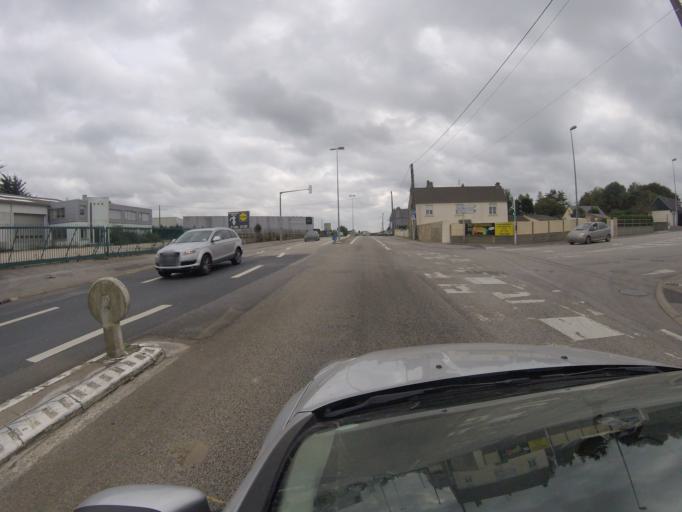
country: FR
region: Lower Normandy
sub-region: Departement de la Manche
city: La Glacerie
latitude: 49.6089
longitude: -1.6001
